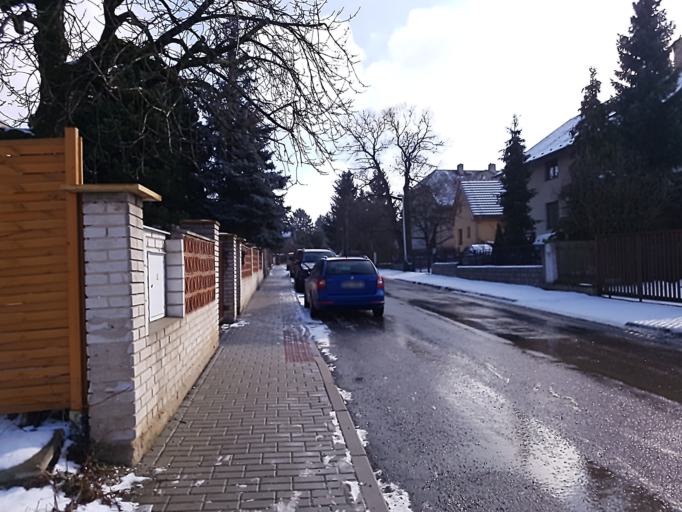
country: CZ
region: Central Bohemia
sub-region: Okres Praha-Vychod
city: Ricany
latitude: 49.9993
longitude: 14.6731
